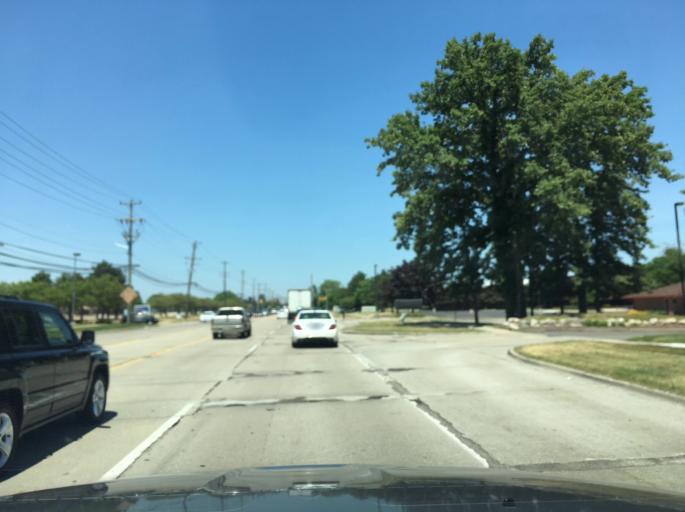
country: US
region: Michigan
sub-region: Macomb County
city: Clinton
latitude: 42.6198
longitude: -82.9531
